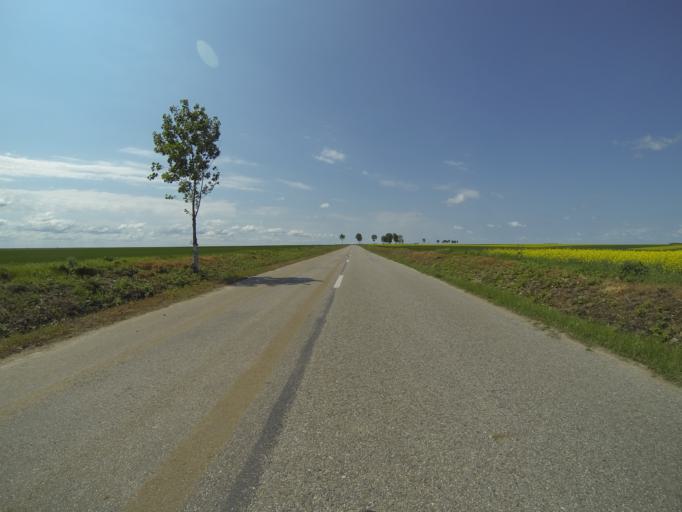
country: RO
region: Dolj
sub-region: Comuna Vartop
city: Vartop
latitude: 44.2196
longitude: 23.3095
